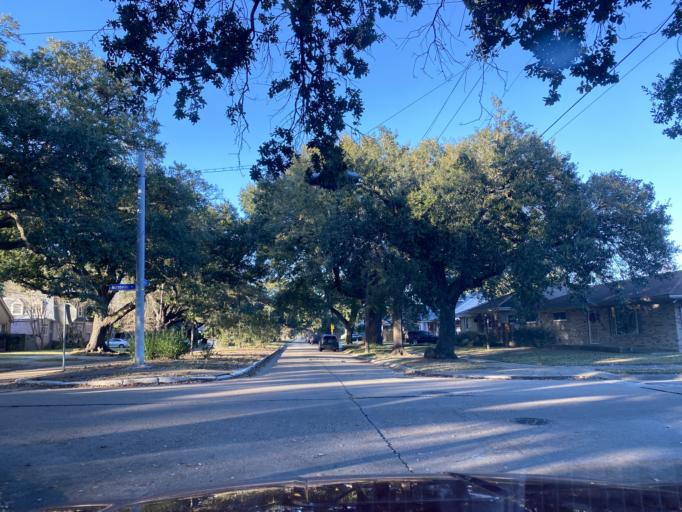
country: US
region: Louisiana
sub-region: Orleans Parish
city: New Orleans
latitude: 30.0084
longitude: -90.0554
